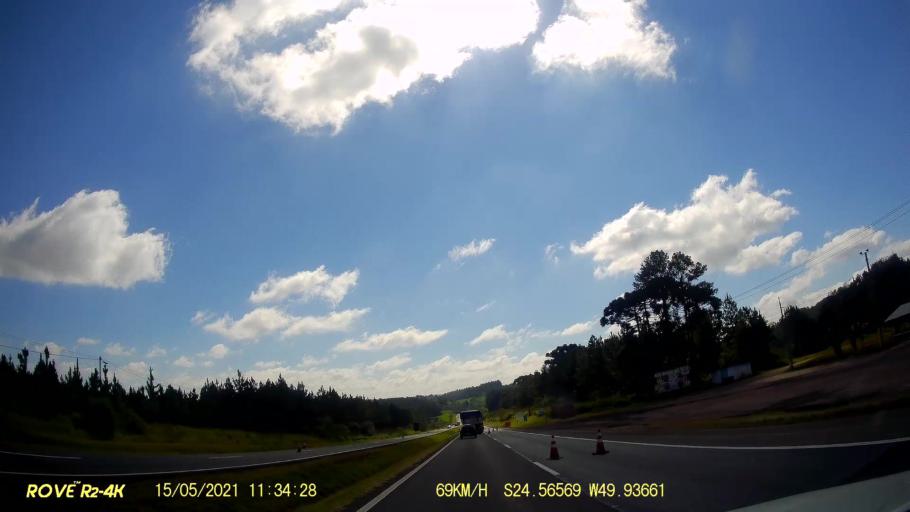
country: BR
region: Parana
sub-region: Pirai Do Sul
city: Pirai do Sul
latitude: -24.5657
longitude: -49.9366
